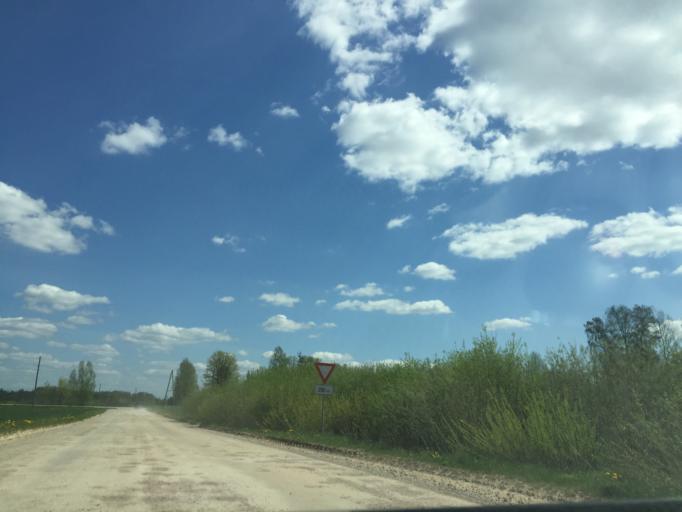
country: LV
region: Vecumnieki
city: Vecumnieki
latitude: 56.5333
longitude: 24.5463
